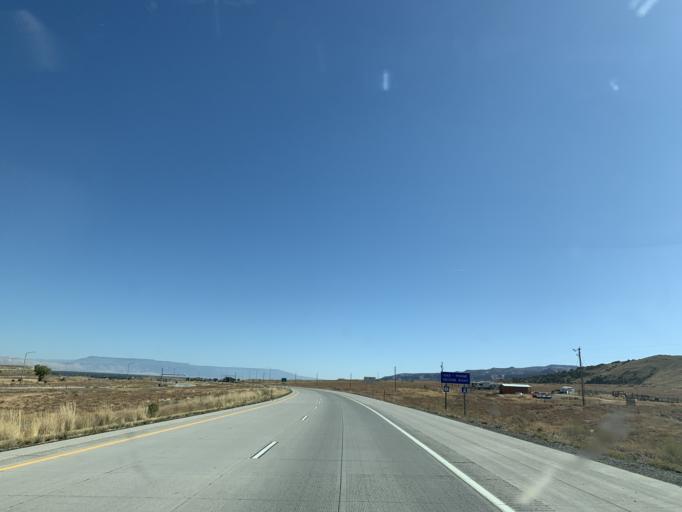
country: US
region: Colorado
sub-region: Mesa County
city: Loma
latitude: 39.1806
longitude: -108.8266
